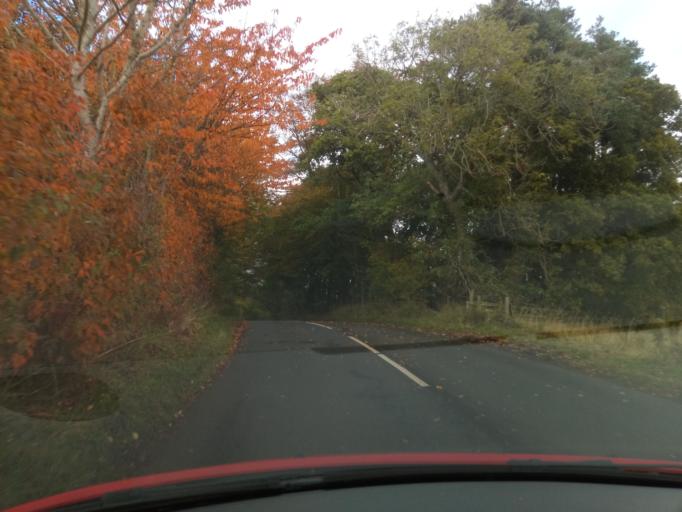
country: GB
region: Scotland
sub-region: The Scottish Borders
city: Newtown St Boswells
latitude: 55.5512
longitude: -2.7051
